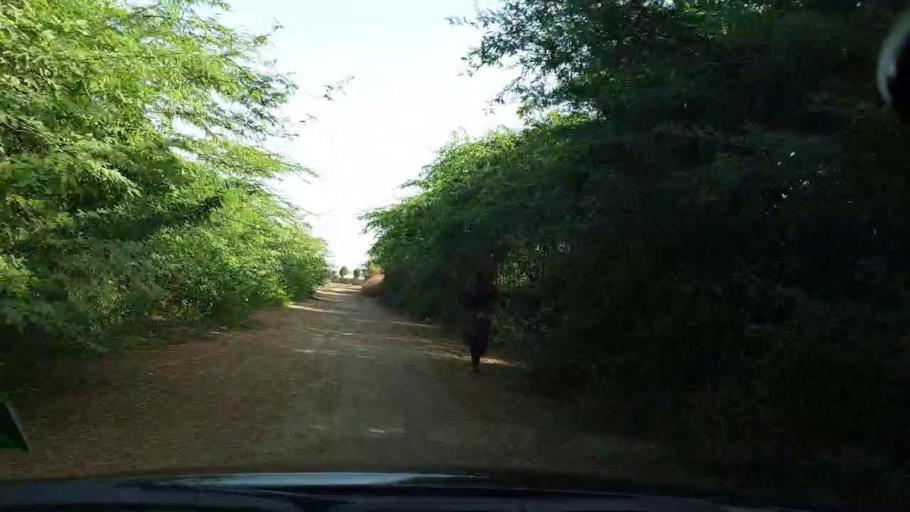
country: PK
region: Sindh
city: Tando Bago
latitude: 24.6592
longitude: 69.0421
